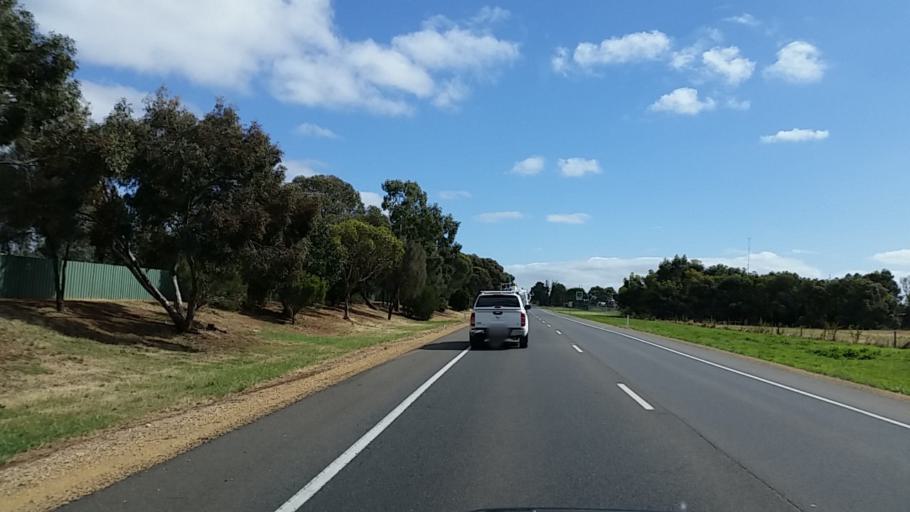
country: AU
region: South Australia
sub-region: Light
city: Roseworthy
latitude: -34.5380
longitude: 138.7500
